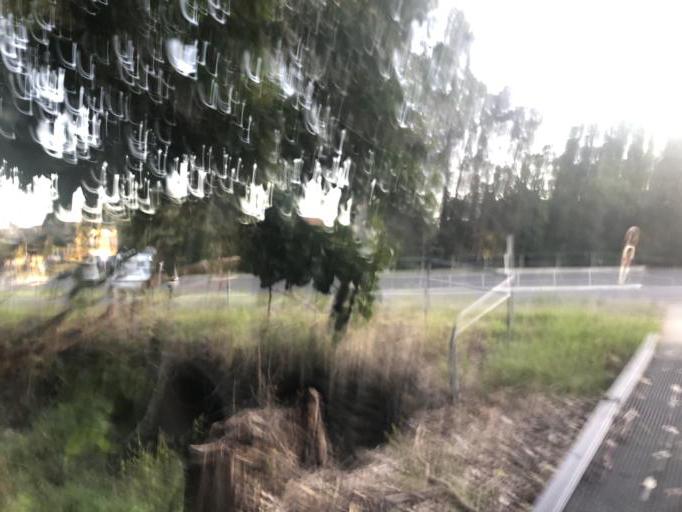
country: AU
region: New South Wales
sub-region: Coffs Harbour
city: Coffs Harbour
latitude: -30.2856
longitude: 153.1309
